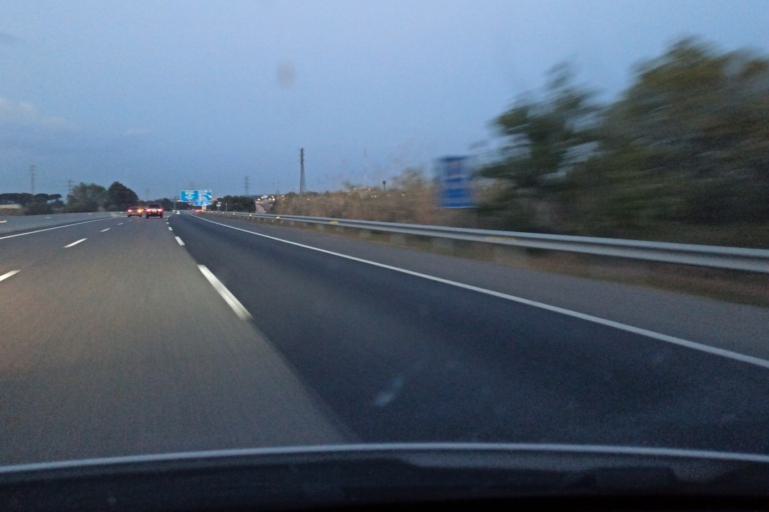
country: ES
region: Catalonia
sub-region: Provincia de Tarragona
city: Vila-seca
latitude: 41.1291
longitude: 1.1598
